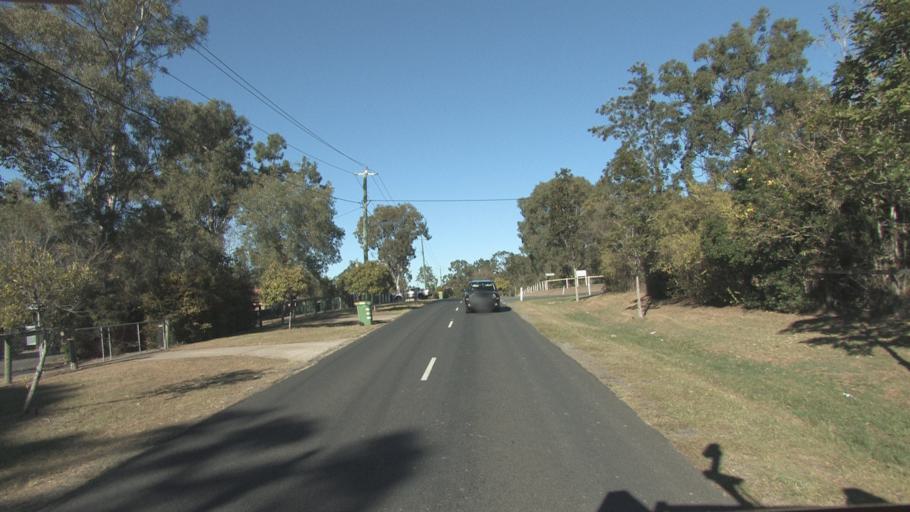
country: AU
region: Queensland
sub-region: Logan
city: North Maclean
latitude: -27.7416
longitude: 152.9681
